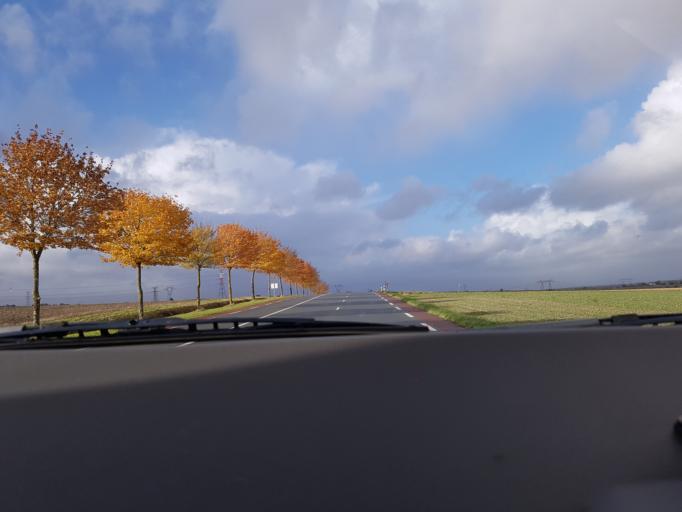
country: FR
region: Poitou-Charentes
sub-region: Departement de la Charente-Maritime
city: Les Gonds
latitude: 45.6634
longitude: -0.5950
